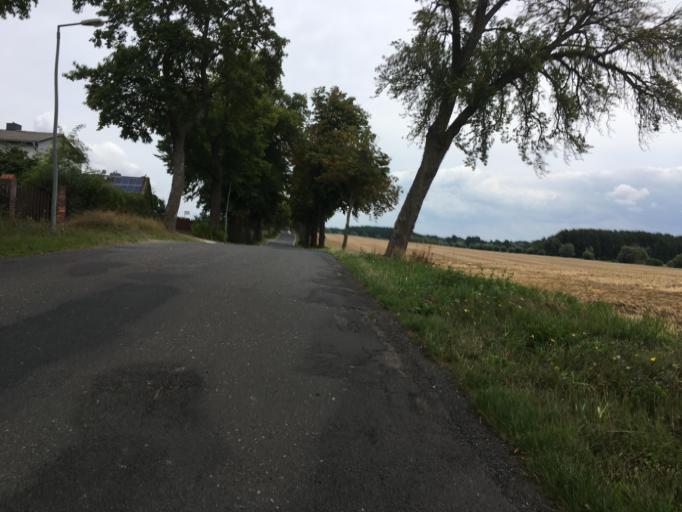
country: DE
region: Brandenburg
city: Prenzlau
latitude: 53.2319
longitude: 13.8432
